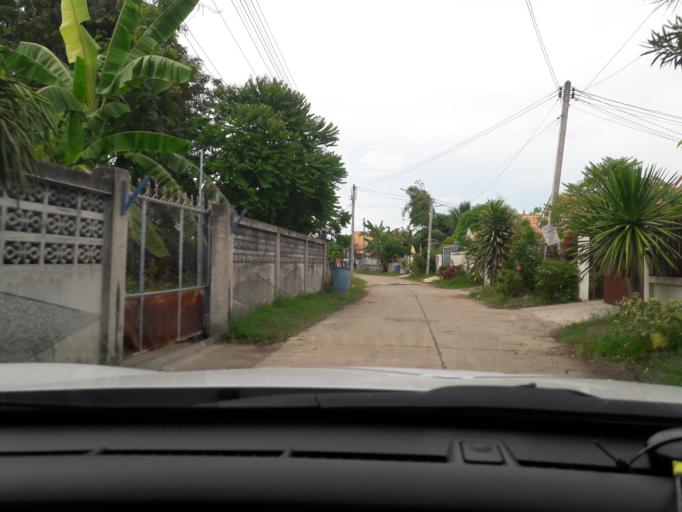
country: TH
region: Nakhon Sawan
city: Tak Fa
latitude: 15.3448
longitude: 100.5022
